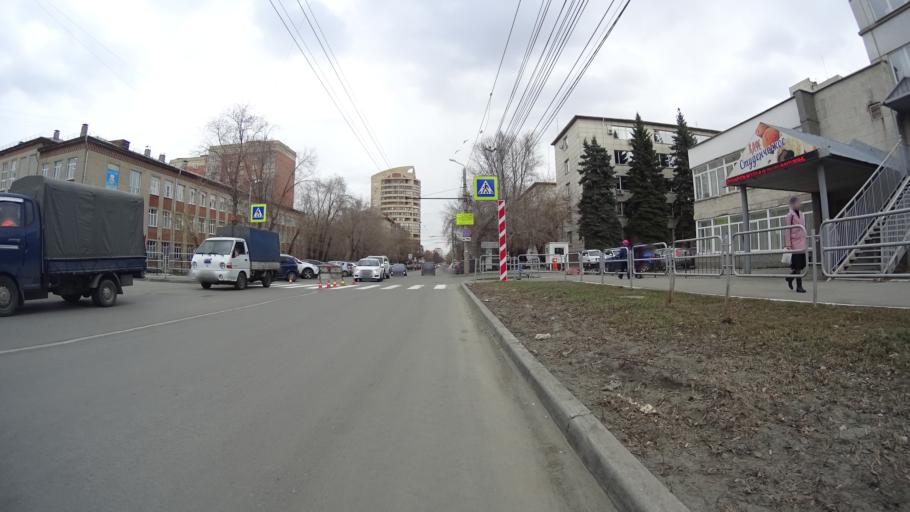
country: RU
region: Chelyabinsk
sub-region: Gorod Chelyabinsk
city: Chelyabinsk
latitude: 55.1574
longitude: 61.3724
